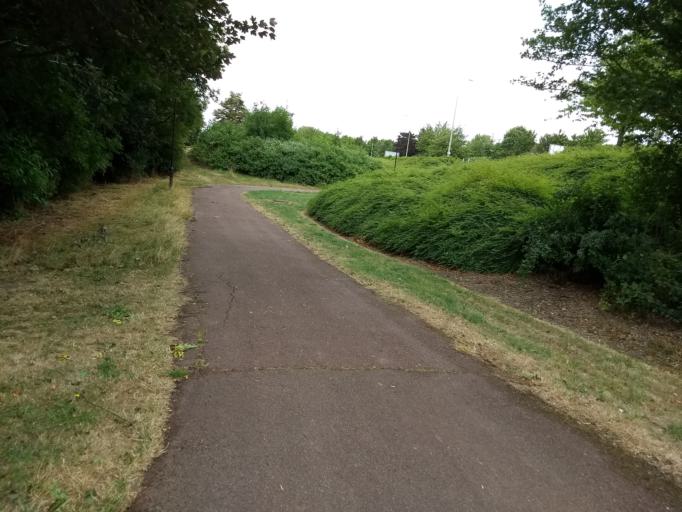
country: GB
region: England
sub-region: Milton Keynes
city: Bradwell
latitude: 52.0586
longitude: -0.7897
